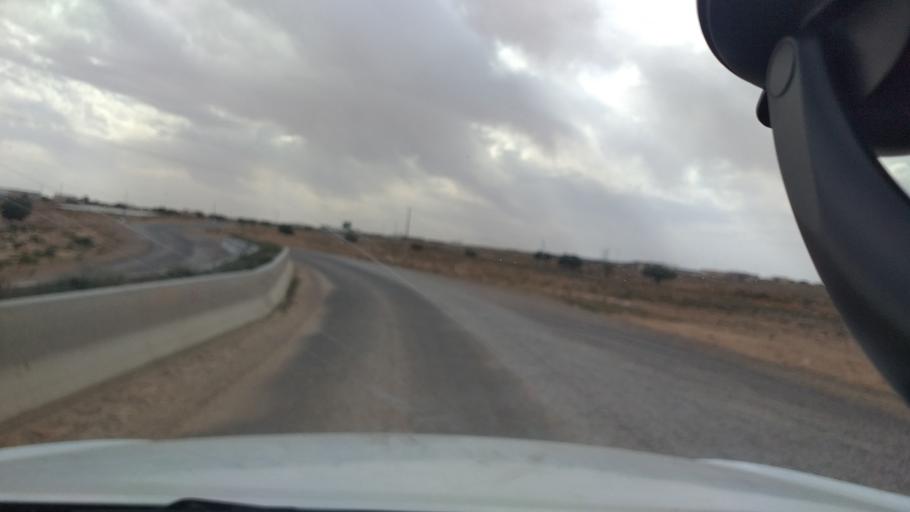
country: TN
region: Madanin
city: Medenine
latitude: 33.2981
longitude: 10.6083
